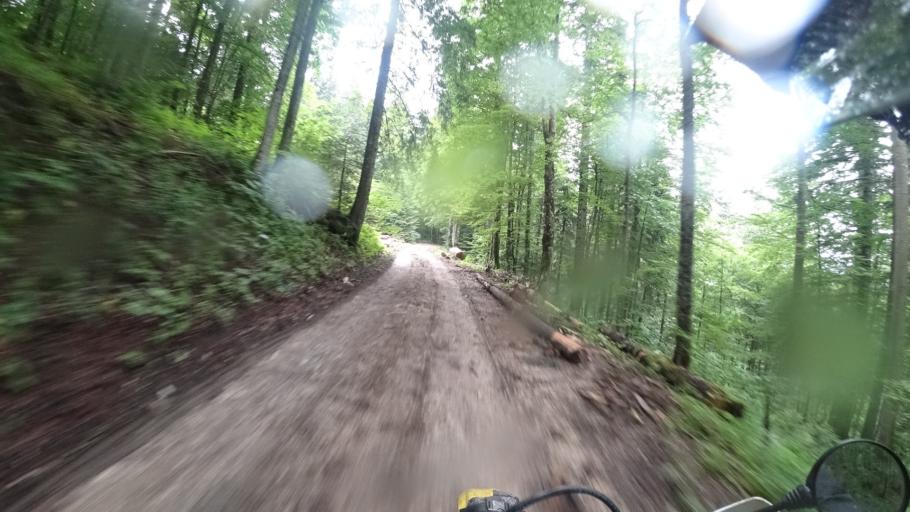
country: HR
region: Primorsko-Goranska
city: Vrbovsko
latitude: 45.2972
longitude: 14.9543
